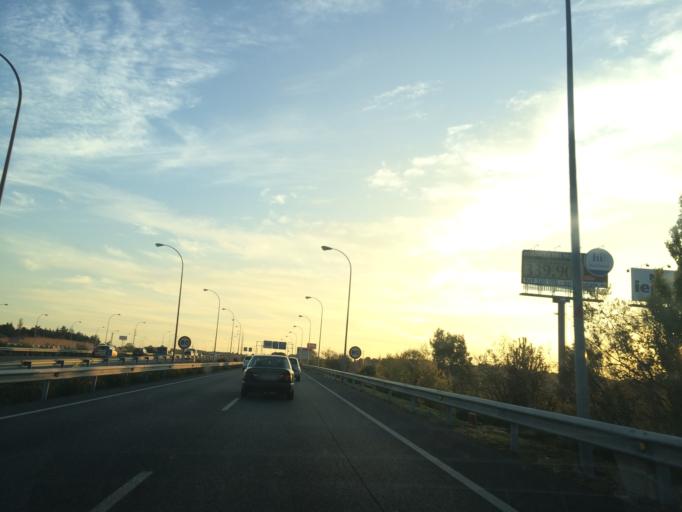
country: ES
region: Madrid
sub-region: Provincia de Madrid
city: Pozuelo de Alarcon
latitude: 40.4365
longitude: -3.8338
